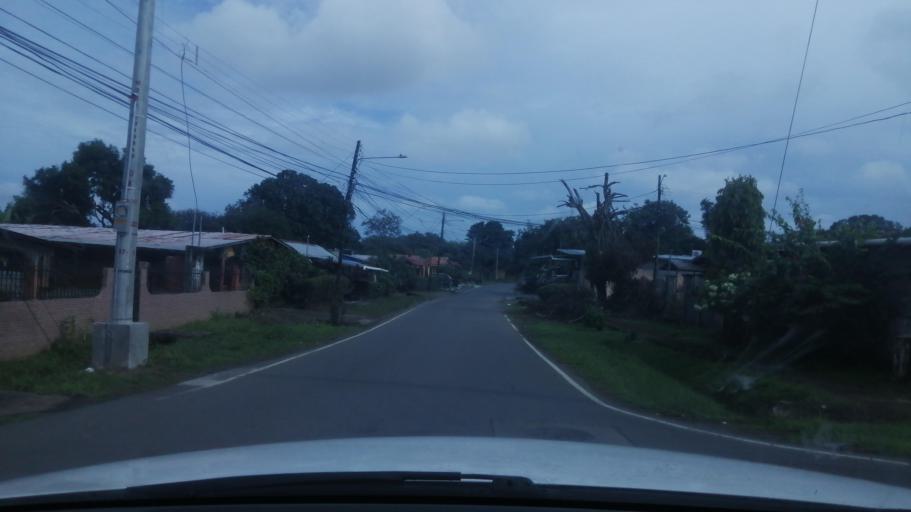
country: PA
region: Chiriqui
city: David
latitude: 8.4043
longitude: -82.4276
